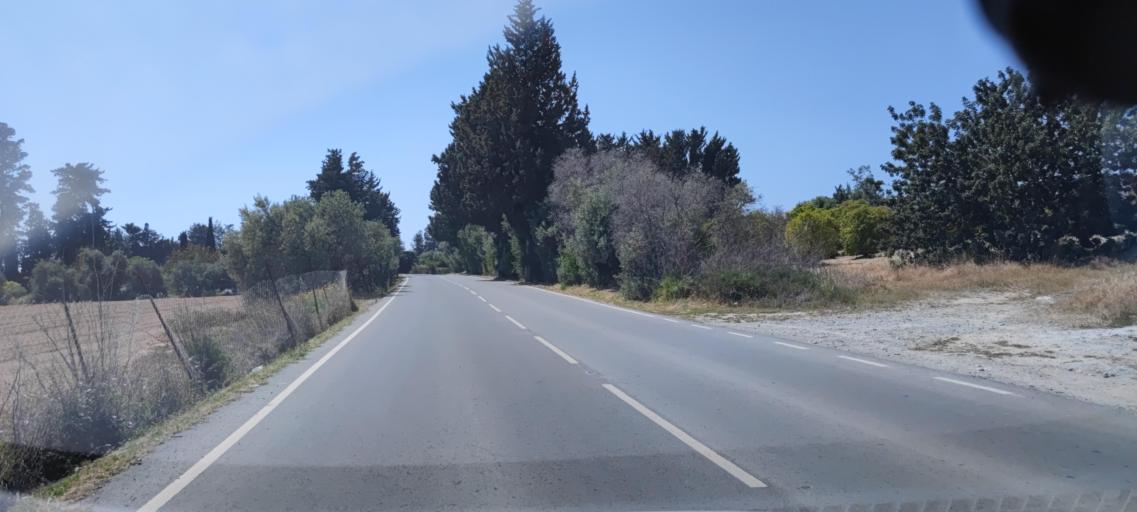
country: CY
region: Larnaka
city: Kolossi
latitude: 34.6536
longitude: 32.9545
